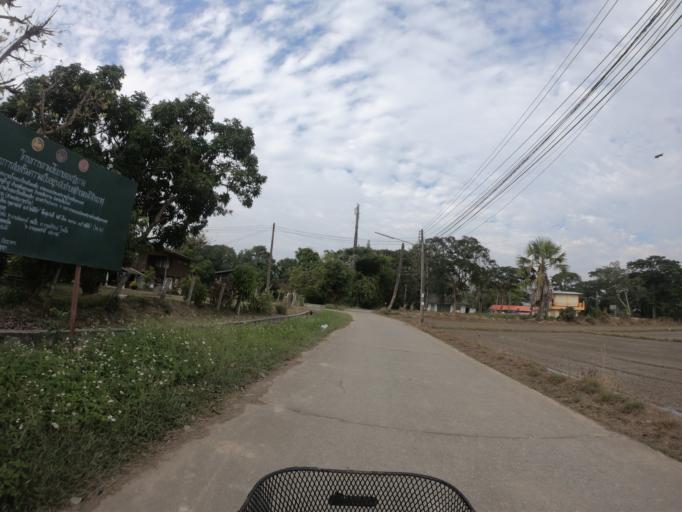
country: TH
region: Chiang Mai
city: San Sai
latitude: 18.7998
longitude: 99.0526
